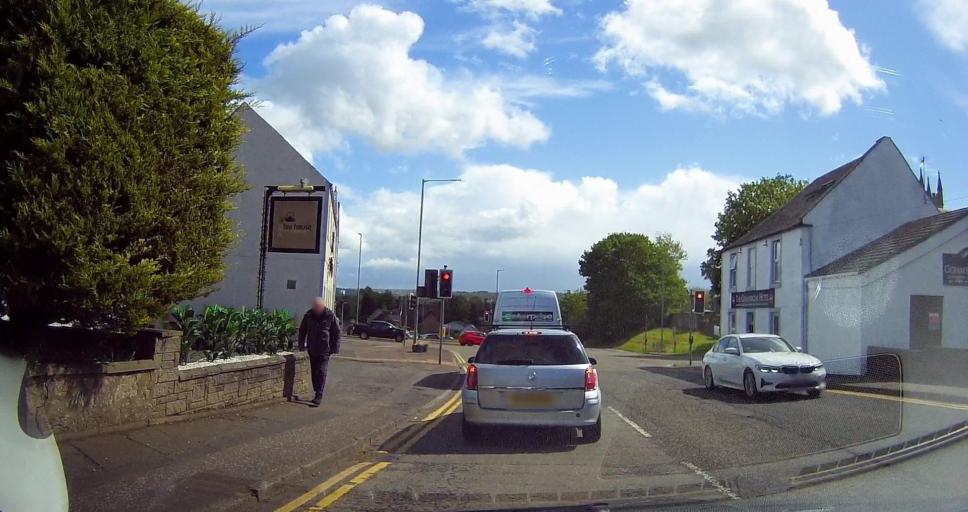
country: GB
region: Scotland
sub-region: Falkirk
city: Larbert
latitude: 56.0202
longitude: -3.8364
